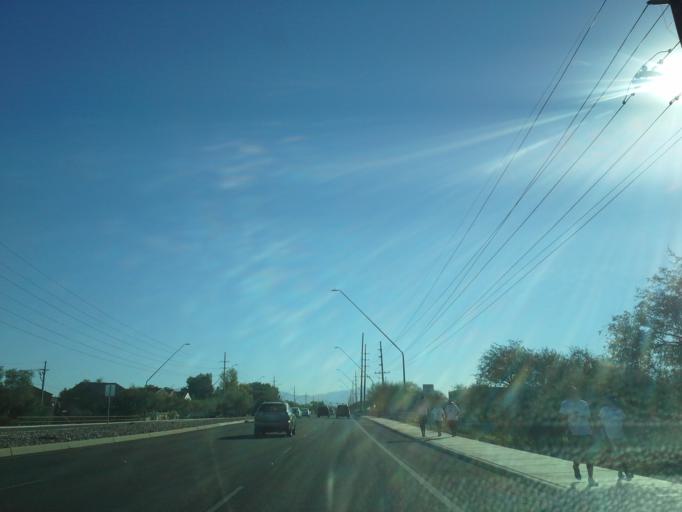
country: US
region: Arizona
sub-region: Pima County
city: Drexel Heights
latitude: 32.1338
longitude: -111.0122
